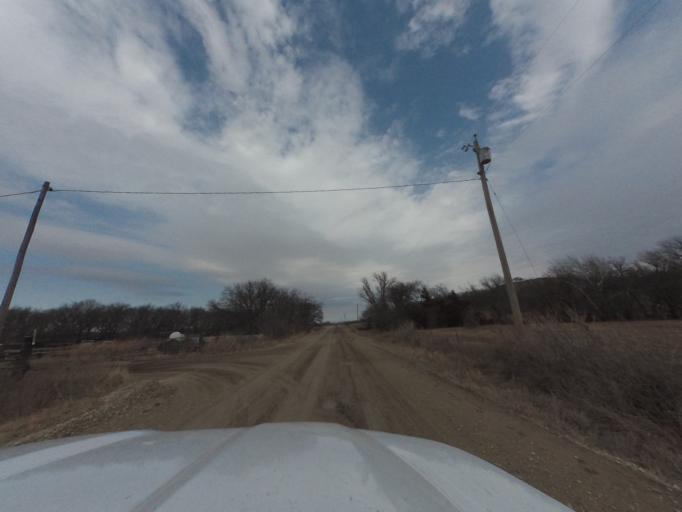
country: US
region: Kansas
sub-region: Chase County
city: Cottonwood Falls
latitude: 38.2866
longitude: -96.7321
